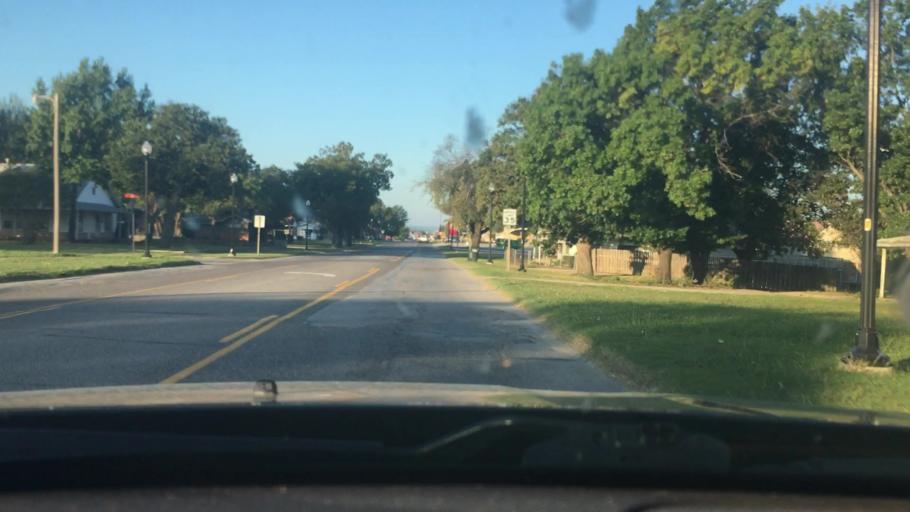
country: US
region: Oklahoma
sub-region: Murray County
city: Davis
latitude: 34.5070
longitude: -97.1121
